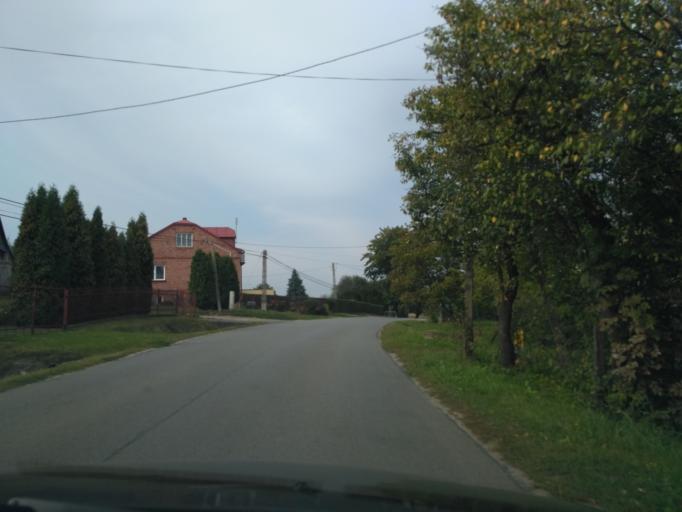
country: PL
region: Subcarpathian Voivodeship
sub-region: Powiat rzeszowski
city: Trzciana
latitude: 50.0561
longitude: 21.8317
